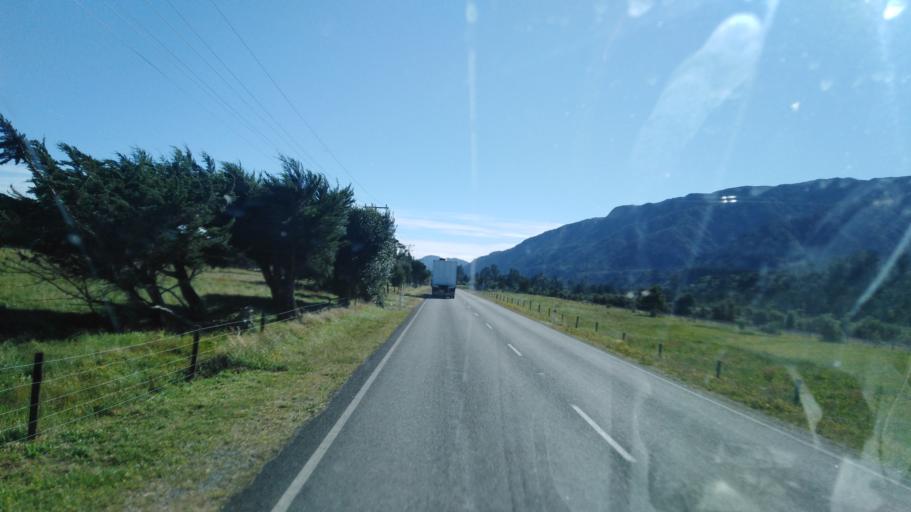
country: NZ
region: West Coast
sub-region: Buller District
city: Westport
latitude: -41.6742
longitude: 171.8006
